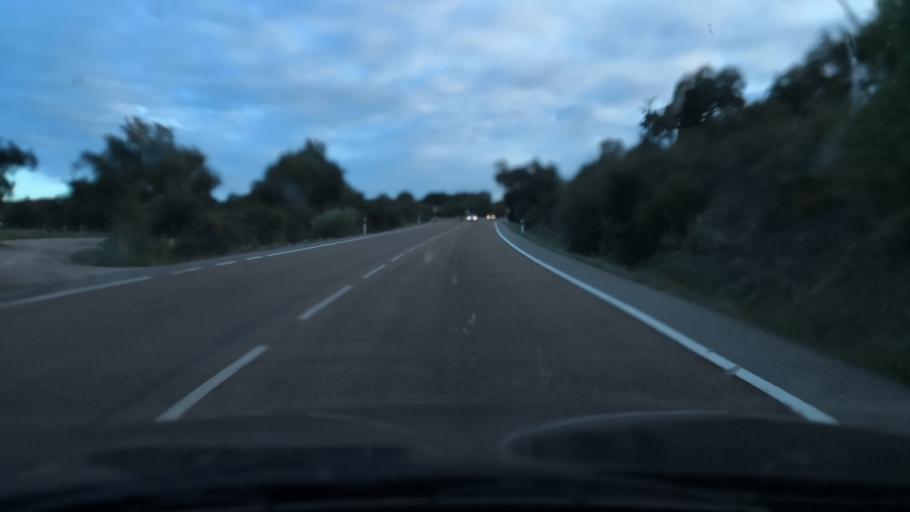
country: ES
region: Extremadura
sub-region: Provincia de Badajoz
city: Puebla de Obando
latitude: 39.2388
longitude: -6.5641
